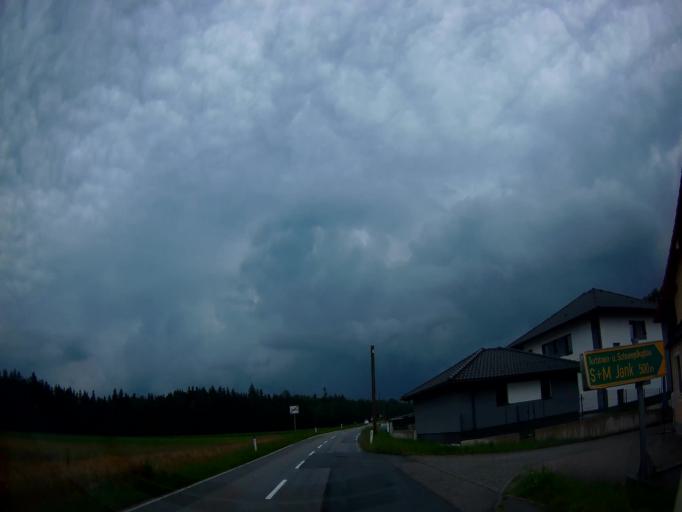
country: AT
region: Salzburg
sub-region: Politischer Bezirk Salzburg-Umgebung
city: Mattsee
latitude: 48.0400
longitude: 13.1474
